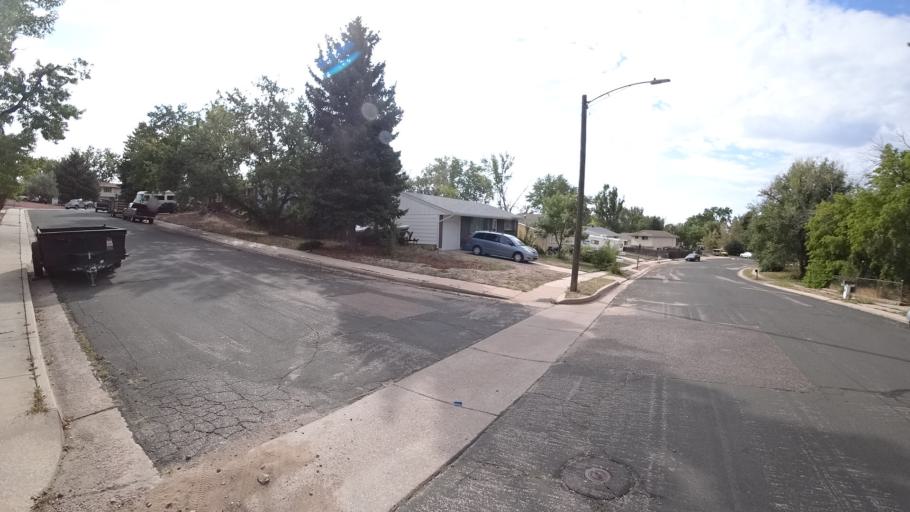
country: US
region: Colorado
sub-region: El Paso County
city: Cimarron Hills
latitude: 38.8425
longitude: -104.7539
